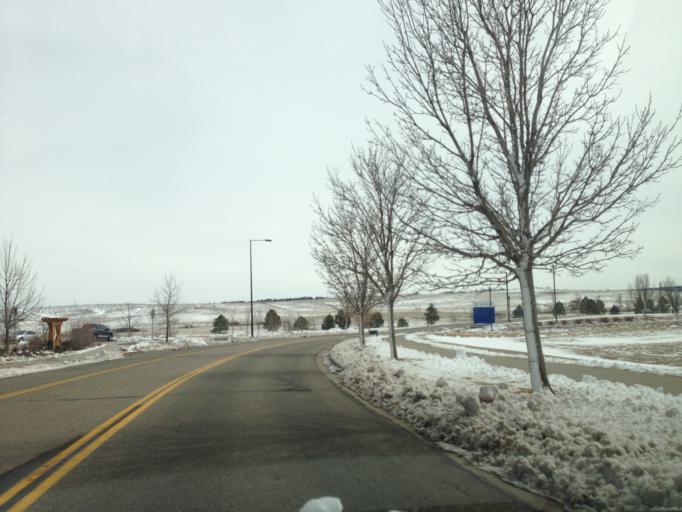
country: US
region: Colorado
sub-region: Boulder County
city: Lafayette
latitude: 39.9718
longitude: -105.0839
